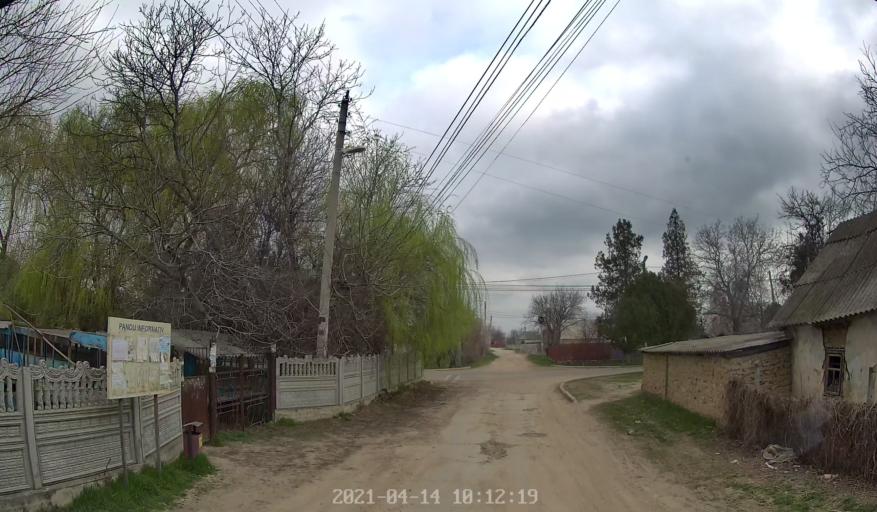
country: MD
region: Criuleni
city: Criuleni
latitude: 47.1479
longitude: 29.1301
